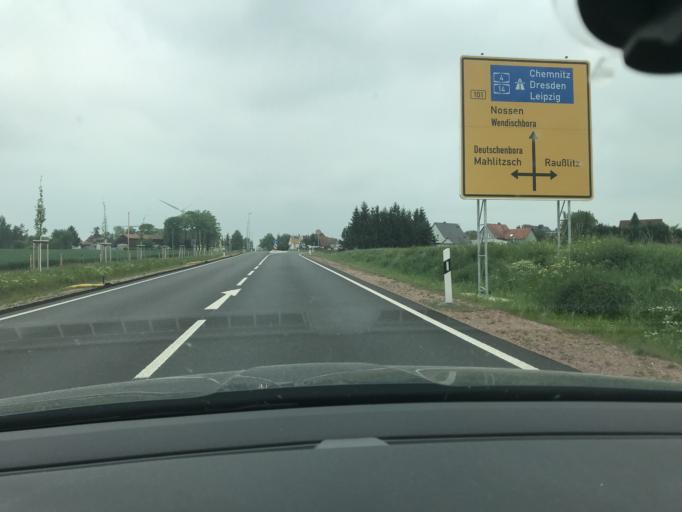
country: DE
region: Saxony
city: Nossen
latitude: 51.0966
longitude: 13.3576
